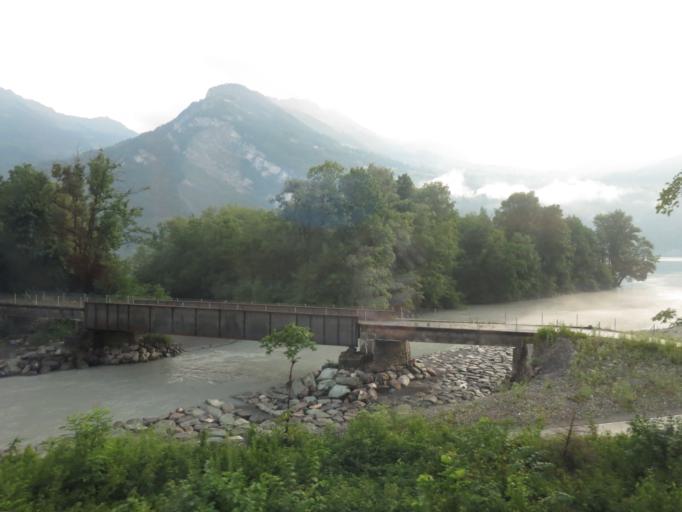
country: CH
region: Saint Gallen
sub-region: Wahlkreis See-Gaster
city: Weesen
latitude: 47.1254
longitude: 9.1176
